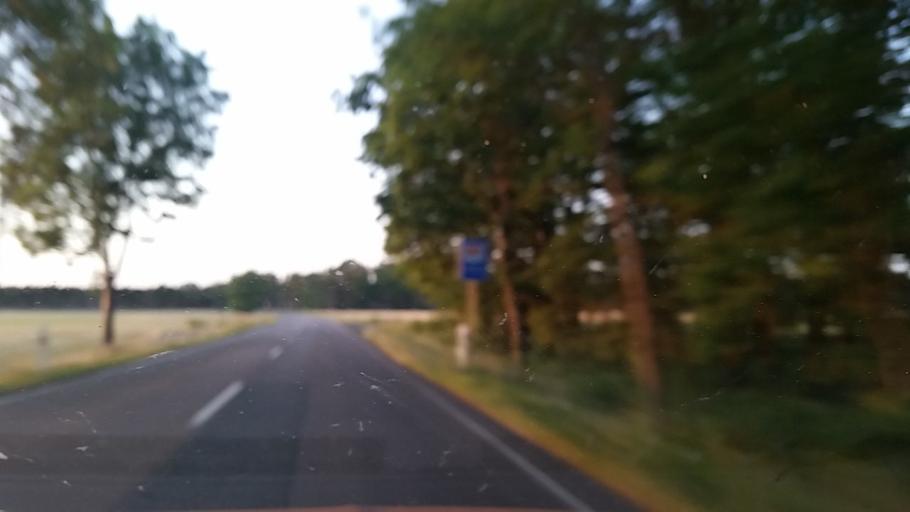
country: DE
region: Saxony-Anhalt
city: Jessen
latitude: 51.7662
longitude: 12.9495
